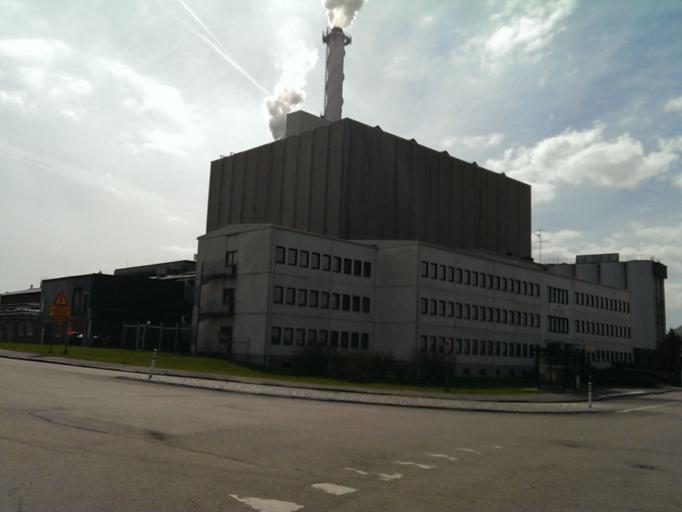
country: SE
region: Skane
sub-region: Bjuvs Kommun
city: Billesholm
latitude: 56.0541
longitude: 12.9712
